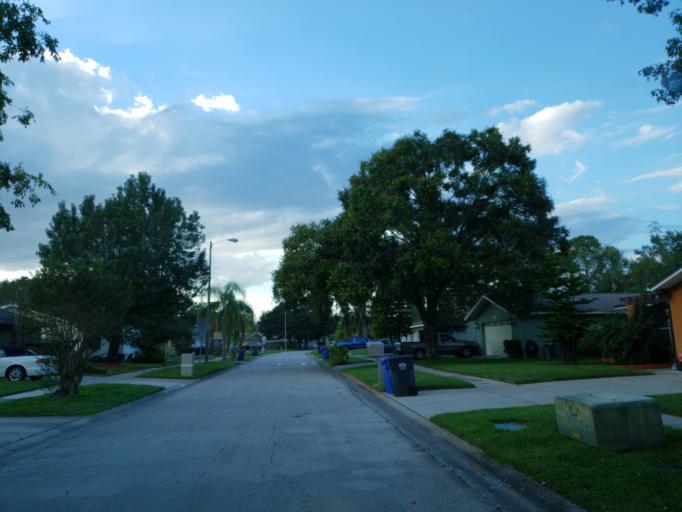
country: US
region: Florida
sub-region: Hillsborough County
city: Carrollwood Village
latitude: 28.0527
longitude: -82.5196
